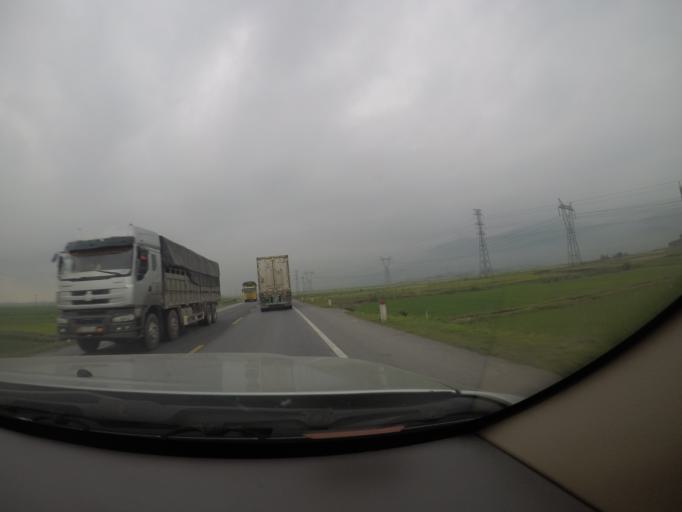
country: VN
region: Ha Tinh
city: Ky Anh
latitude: 18.0967
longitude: 106.2603
